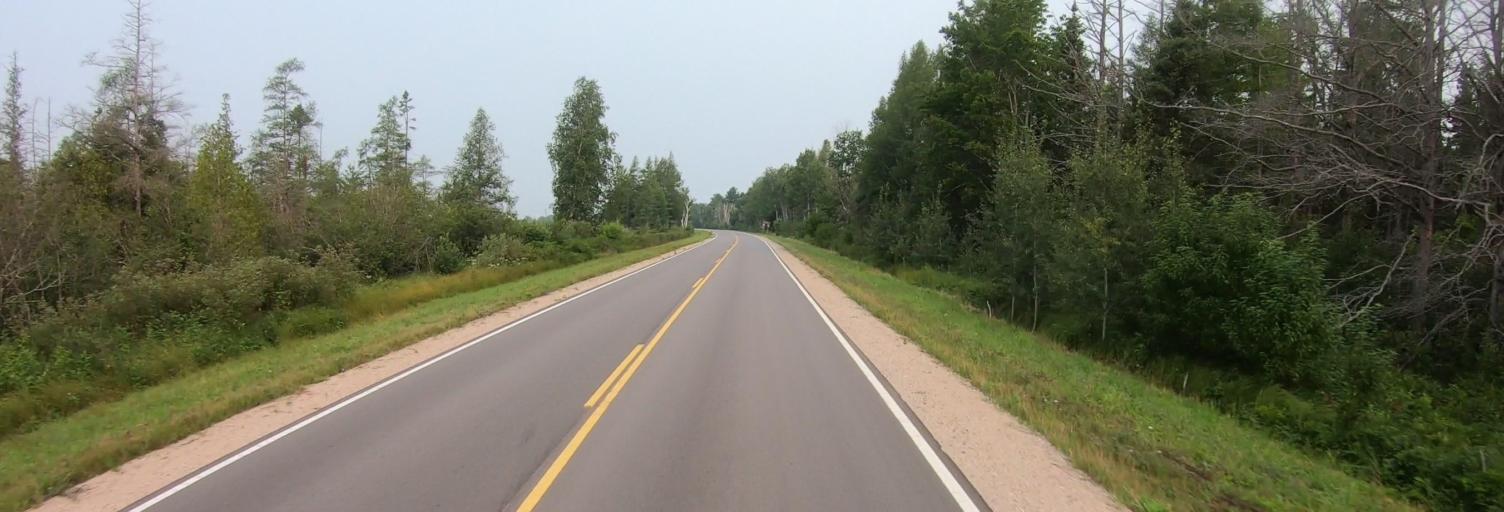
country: US
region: Michigan
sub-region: Luce County
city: Newberry
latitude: 46.4753
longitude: -84.9793
